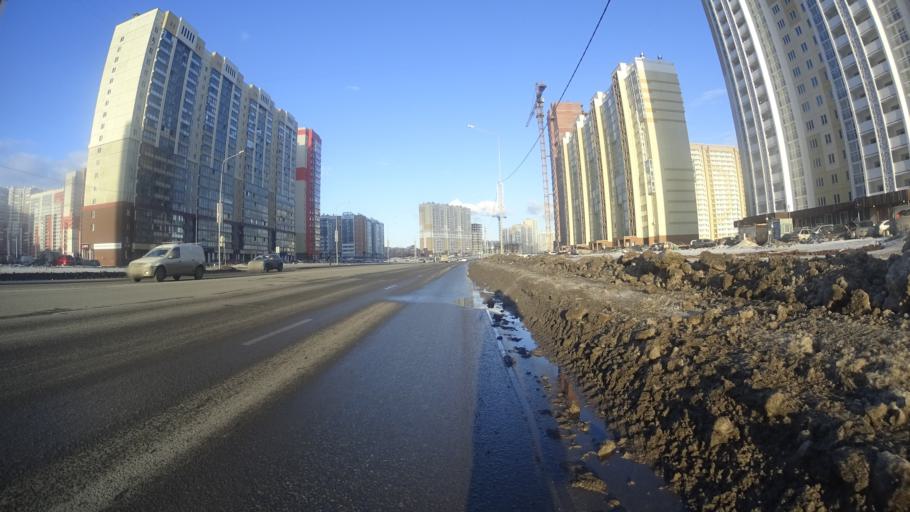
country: RU
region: Chelyabinsk
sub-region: Gorod Chelyabinsk
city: Chelyabinsk
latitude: 55.1721
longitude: 61.3133
